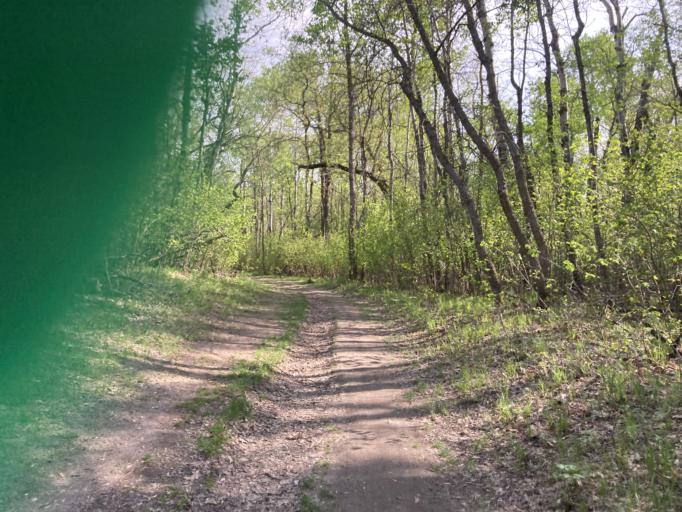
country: CA
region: Manitoba
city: Brandon
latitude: 49.7203
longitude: -99.9062
